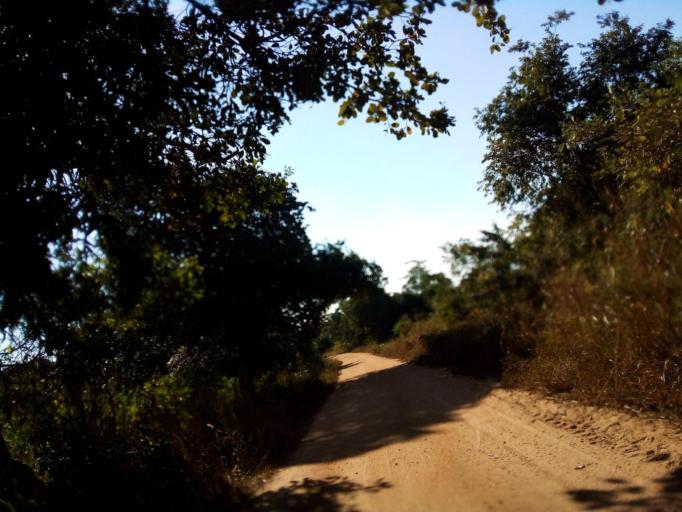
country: MZ
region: Zambezia
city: Quelimane
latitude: -17.5183
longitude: 36.6087
